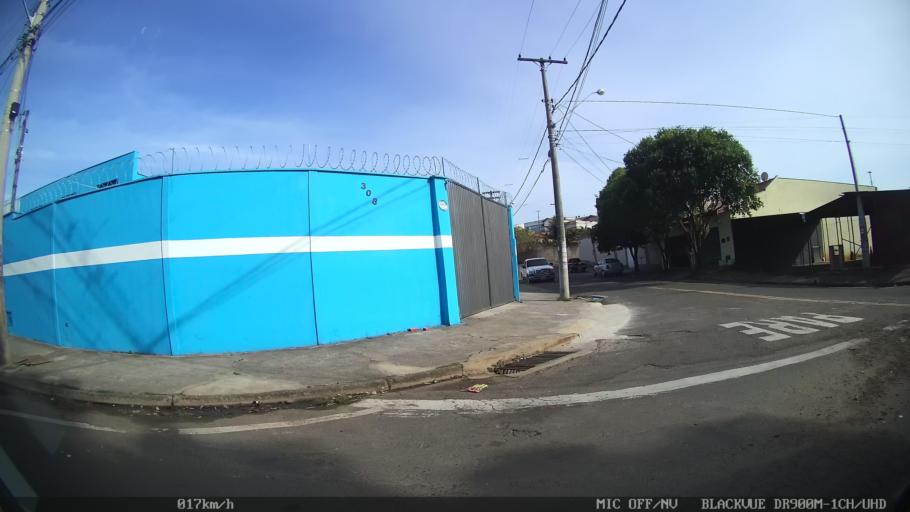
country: BR
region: Sao Paulo
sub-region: Piracicaba
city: Piracicaba
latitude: -22.7379
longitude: -47.6690
